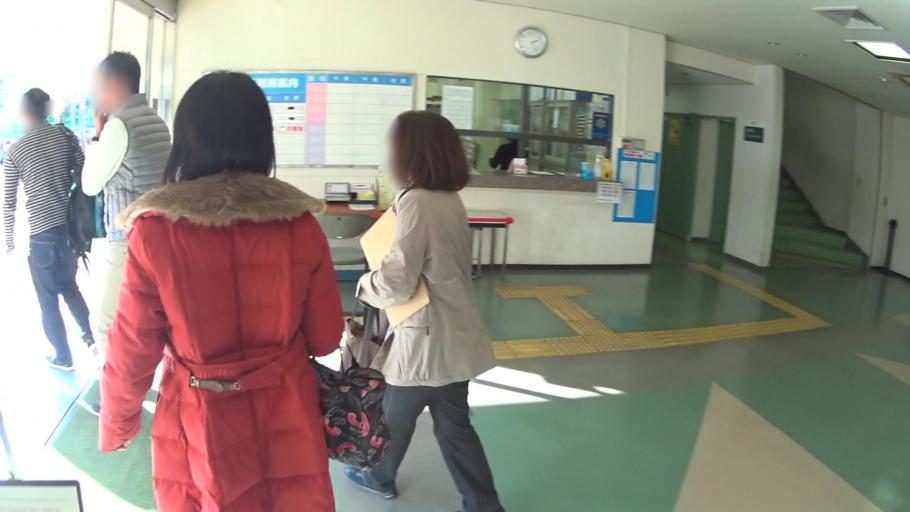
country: JP
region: Osaka
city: Osaka-shi
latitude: 34.6543
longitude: 135.5335
